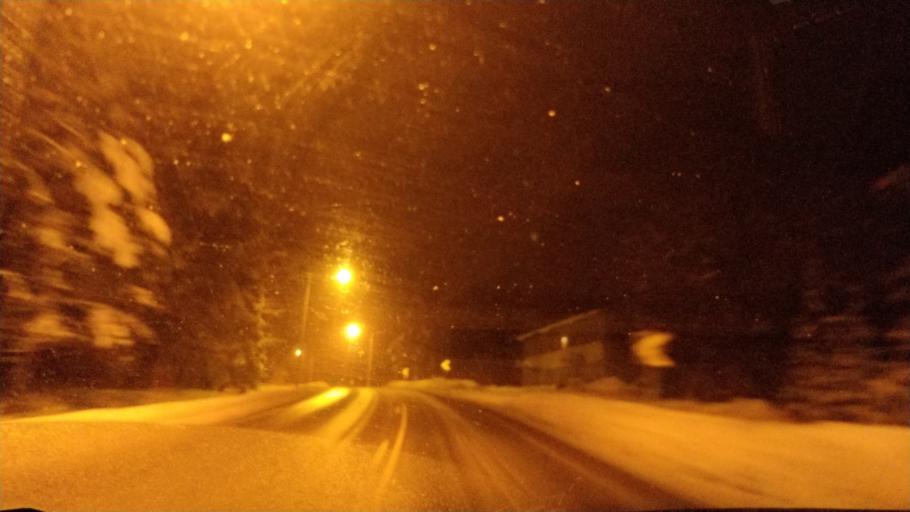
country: FI
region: Lapland
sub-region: Rovaniemi
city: Rovaniemi
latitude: 66.2752
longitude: 25.3302
